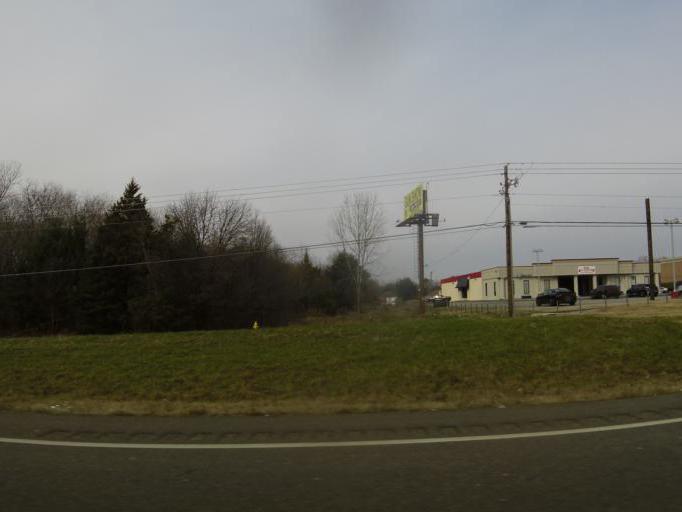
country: US
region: Alabama
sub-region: Montgomery County
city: Montgomery
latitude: 32.3370
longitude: -86.2281
